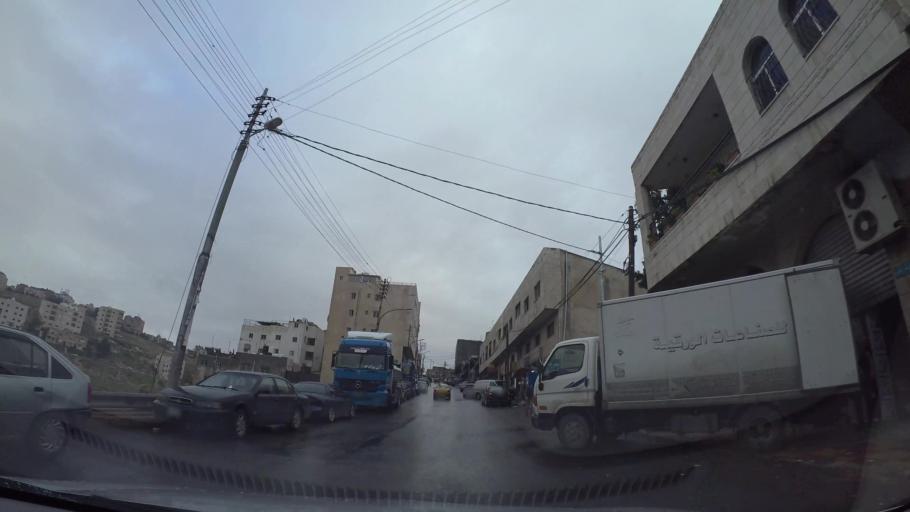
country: JO
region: Amman
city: Al Jubayhah
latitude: 32.0287
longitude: 35.8387
